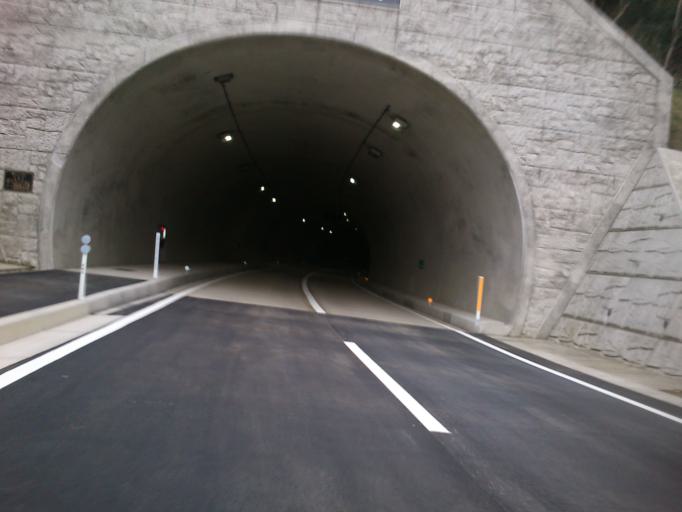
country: JP
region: Kyoto
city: Miyazu
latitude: 35.7444
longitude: 135.2559
